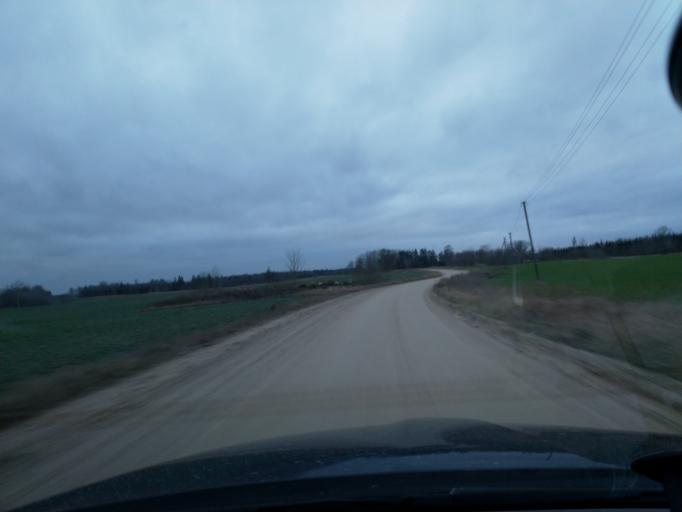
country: LV
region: Saldus Rajons
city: Saldus
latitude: 56.8963
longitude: 22.3146
